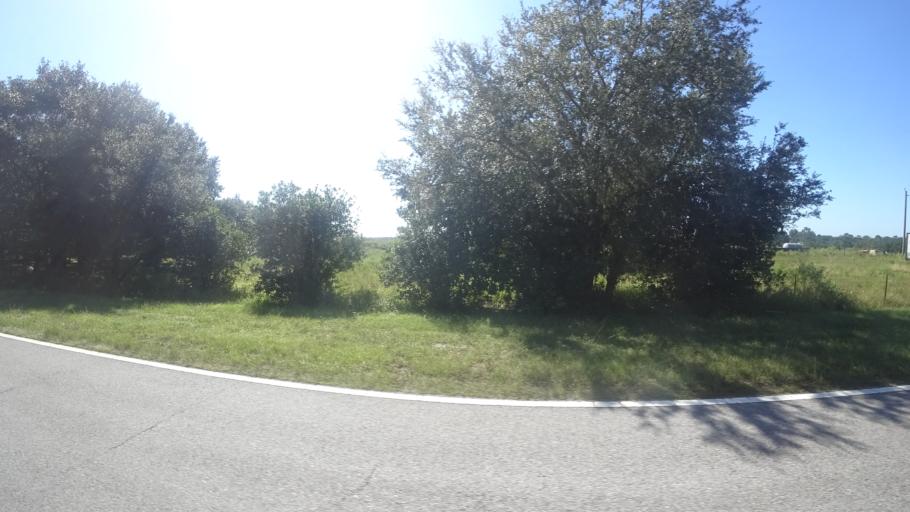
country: US
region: Florida
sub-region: Sarasota County
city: Lake Sarasota
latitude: 27.3503
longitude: -82.2473
